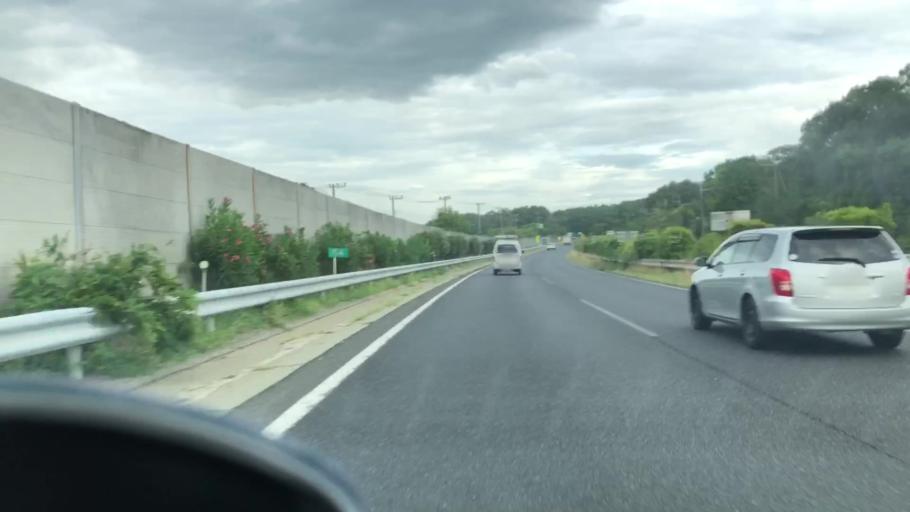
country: JP
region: Hyogo
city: Yashiro
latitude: 34.9175
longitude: 135.0200
